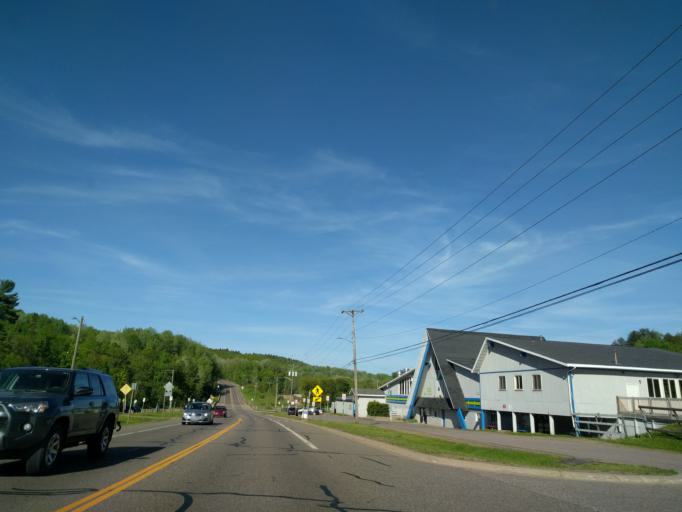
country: US
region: Michigan
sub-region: Marquette County
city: Marquette
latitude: 46.5084
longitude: -87.4215
